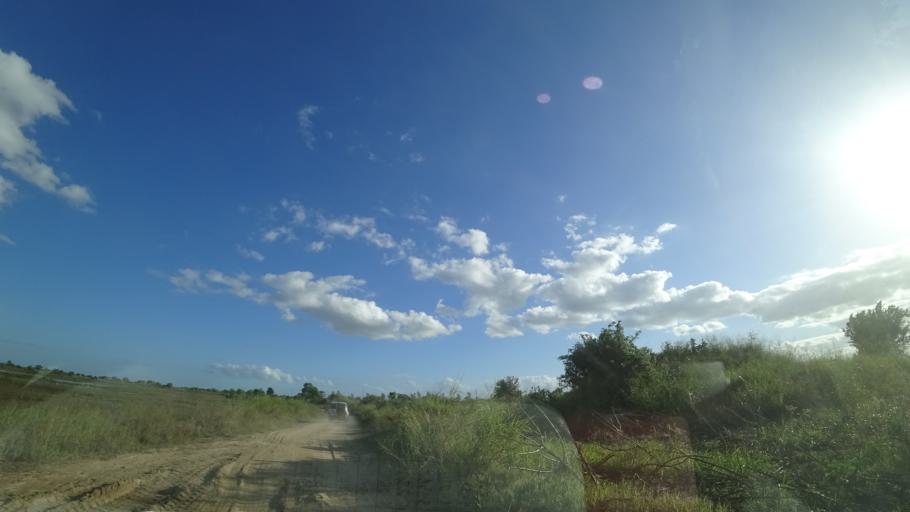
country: MZ
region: Sofala
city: Dondo
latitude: -19.4252
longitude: 34.5621
